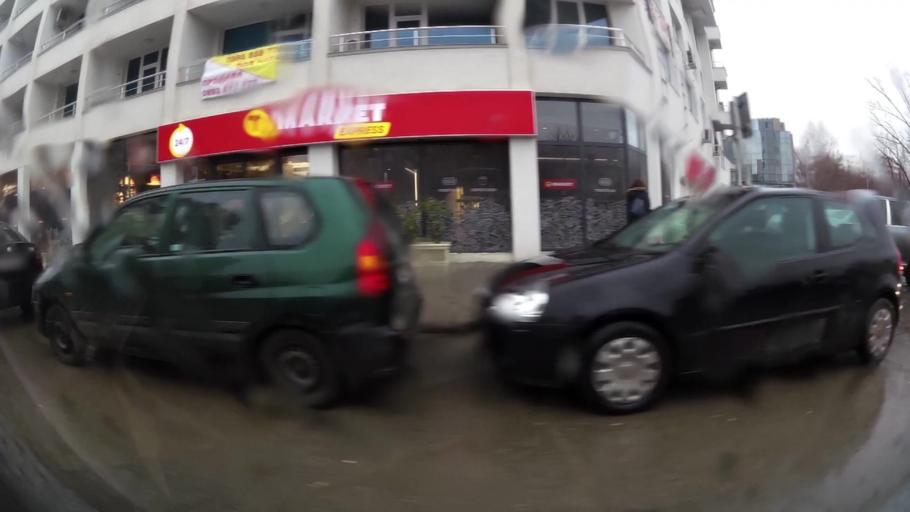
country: BG
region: Sofia-Capital
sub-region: Stolichna Obshtina
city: Sofia
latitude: 42.6458
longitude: 23.3421
